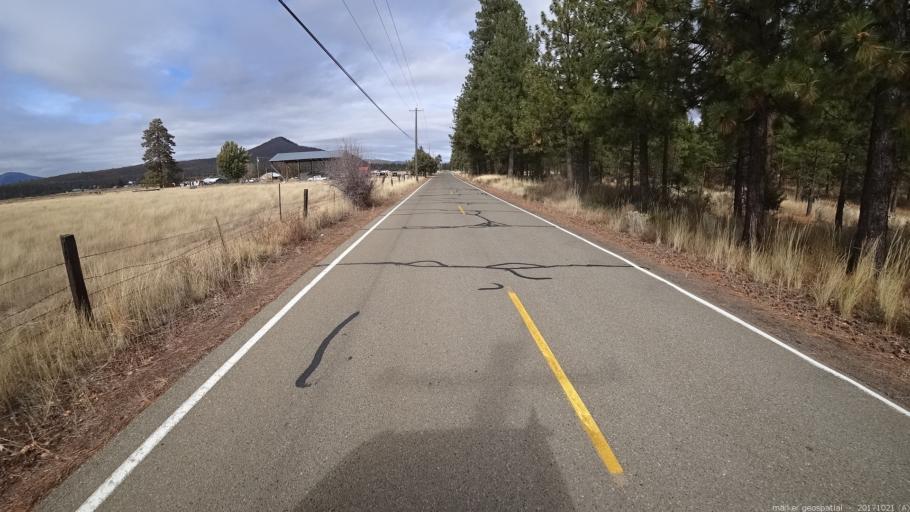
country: US
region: California
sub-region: Shasta County
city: Burney
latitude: 40.9146
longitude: -121.6469
